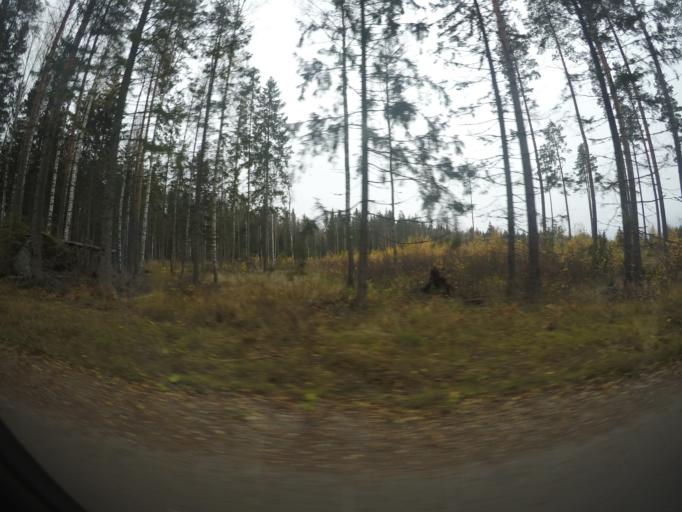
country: SE
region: Vaestmanland
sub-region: Surahammars Kommun
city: Ramnas
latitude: 59.7370
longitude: 16.1181
